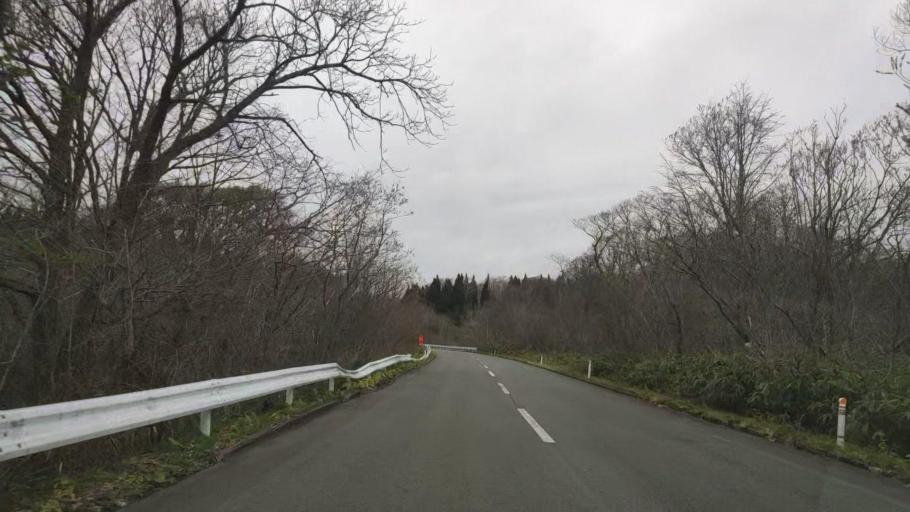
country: JP
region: Akita
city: Hanawa
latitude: 40.4097
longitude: 140.8487
